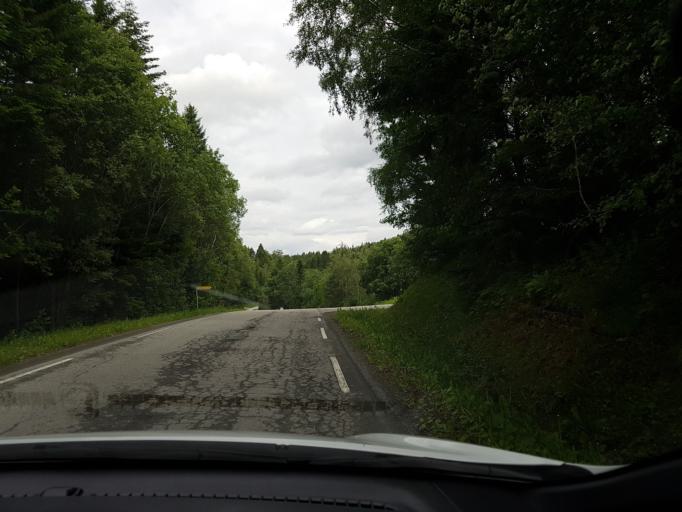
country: NO
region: Nord-Trondelag
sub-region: Levanger
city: Skogn
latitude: 63.6246
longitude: 11.1626
